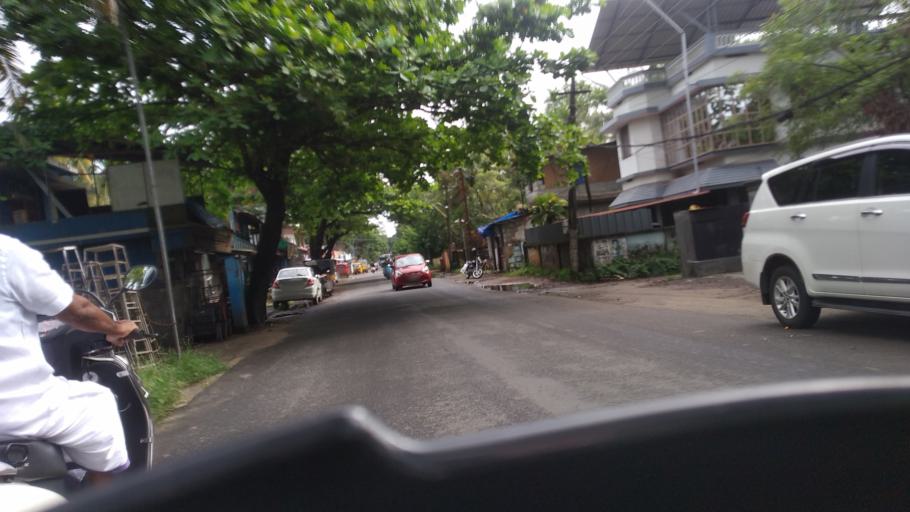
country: IN
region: Kerala
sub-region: Ernakulam
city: Elur
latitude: 10.0881
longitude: 76.2084
